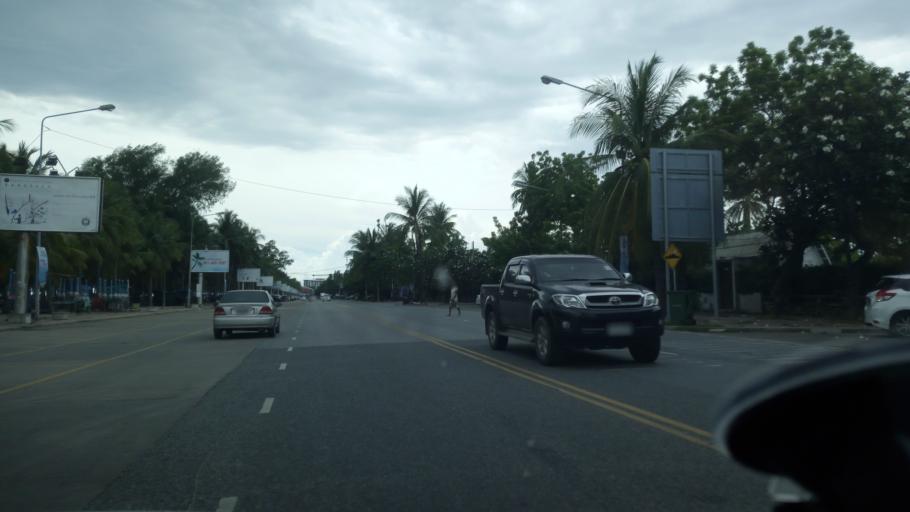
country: TH
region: Chon Buri
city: Chon Buri
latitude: 13.2931
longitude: 100.9078
